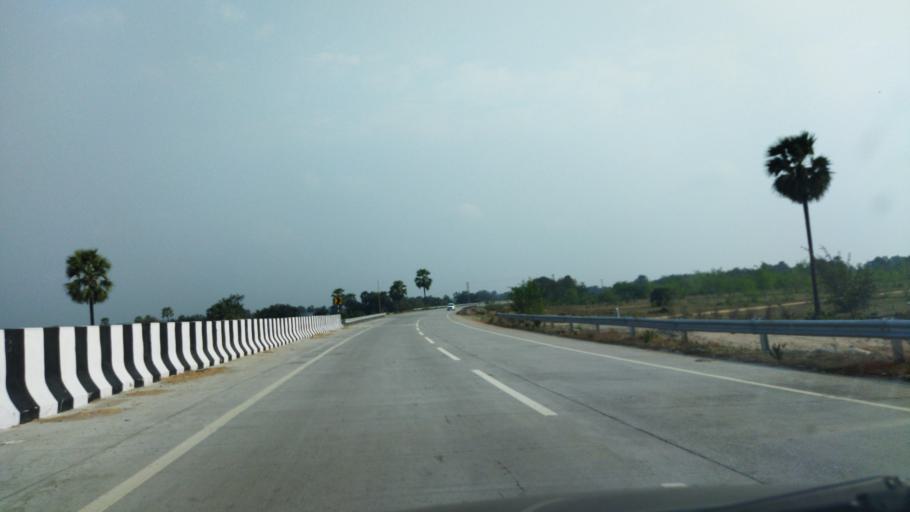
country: IN
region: Telangana
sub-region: Nalgonda
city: Nalgonda
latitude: 17.1719
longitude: 79.3957
